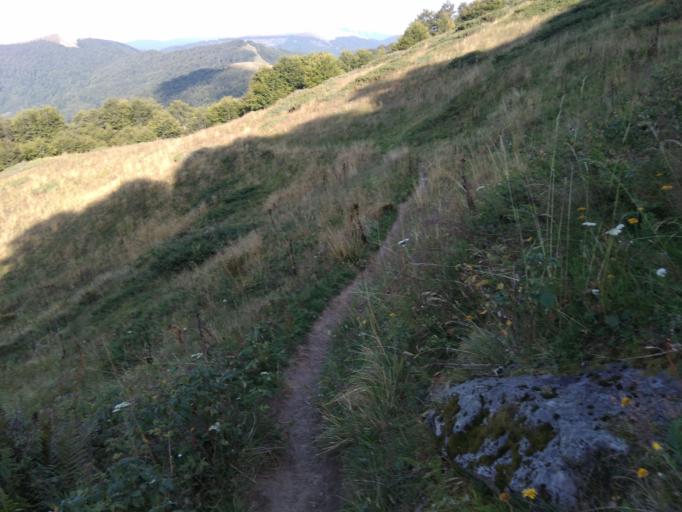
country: BG
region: Stara Zagora
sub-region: Obshtina Pavel Banya
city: Asen
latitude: 42.7617
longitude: 25.1104
